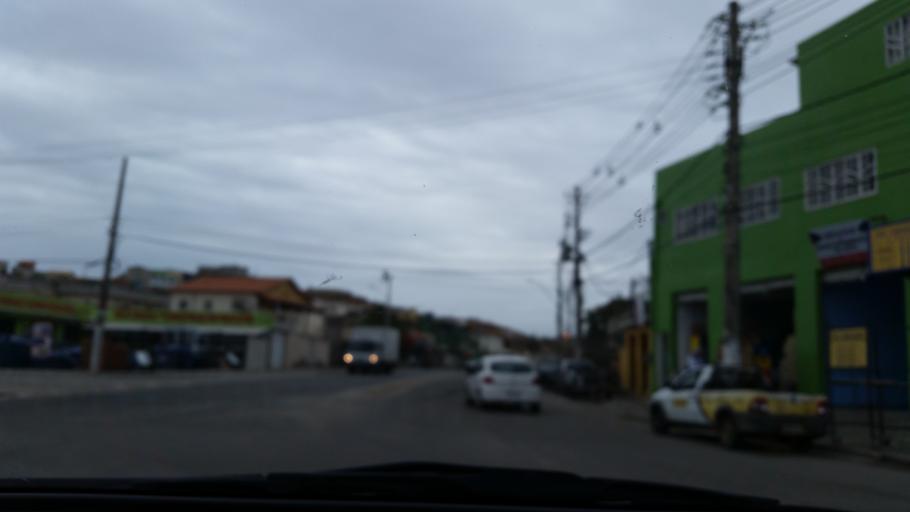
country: BR
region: Rio de Janeiro
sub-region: Cabo Frio
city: Cabo Frio
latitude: -22.8556
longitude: -42.0454
